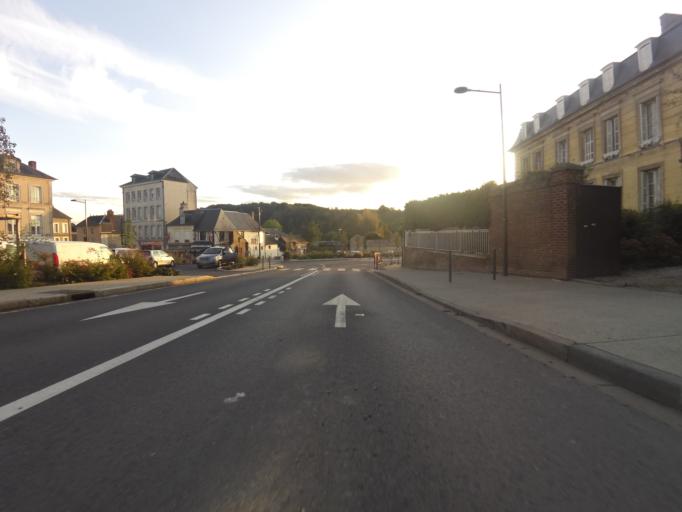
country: FR
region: Lower Normandy
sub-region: Departement du Calvados
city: La Vespiere
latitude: 49.0239
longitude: 0.4059
